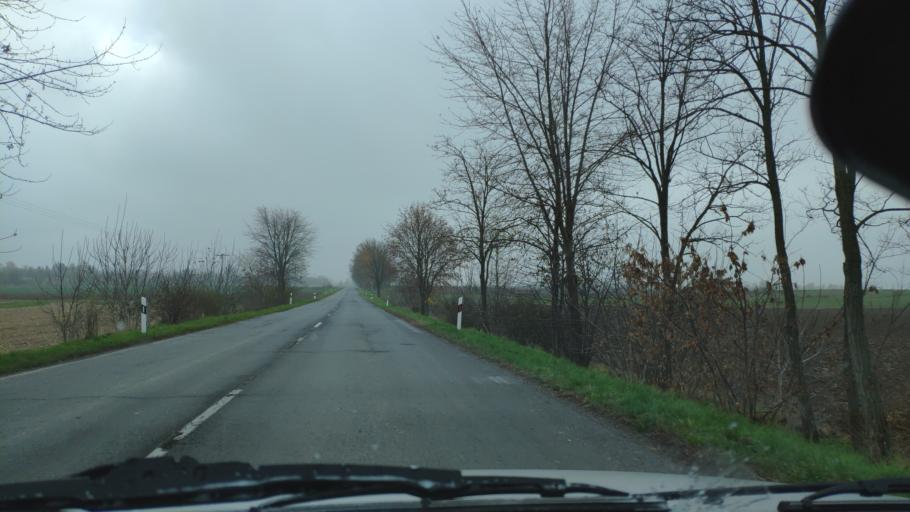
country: HU
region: Zala
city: Zalakomar
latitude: 46.5965
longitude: 17.2634
